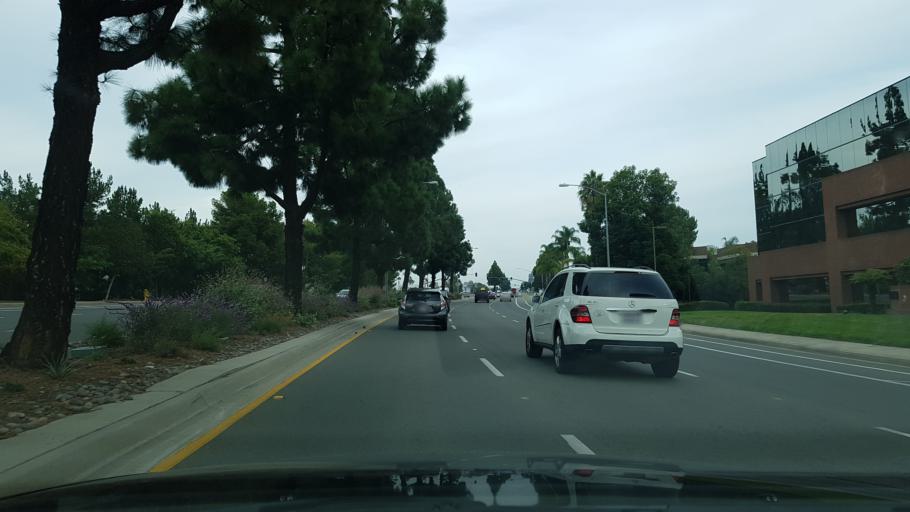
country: US
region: California
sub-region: San Diego County
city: Fairbanks Ranch
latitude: 32.9060
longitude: -117.1797
